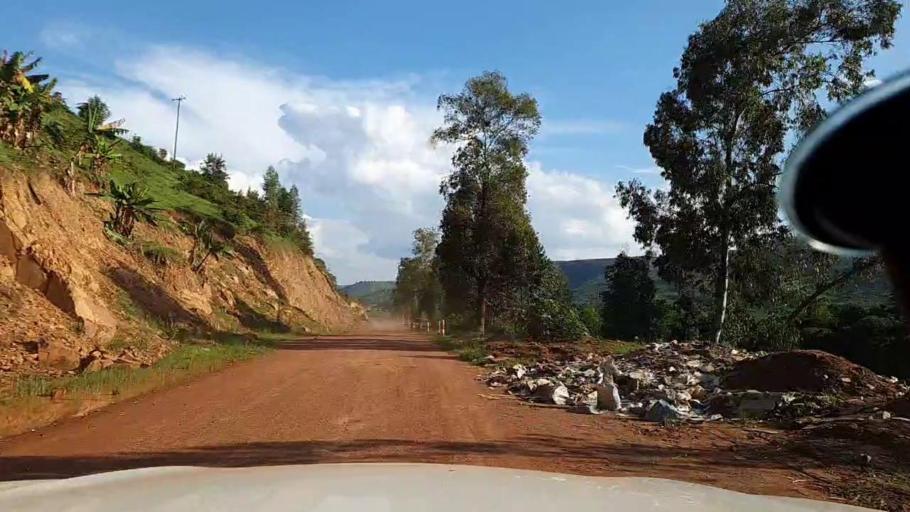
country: RW
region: Kigali
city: Kigali
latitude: -1.8702
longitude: 29.9315
